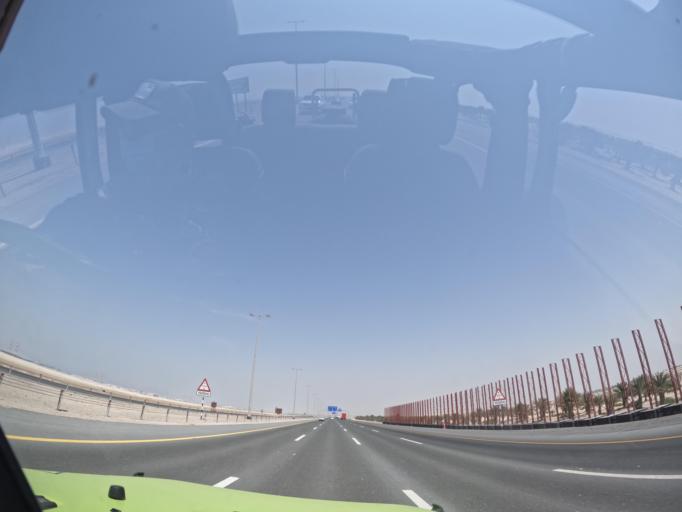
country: AE
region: Abu Dhabi
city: Abu Dhabi
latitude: 24.2368
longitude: 54.4628
